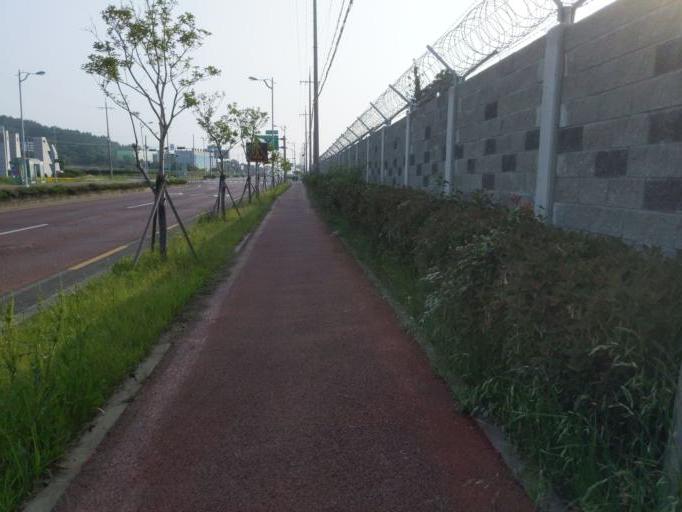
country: KR
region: Jeju-do
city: Gaigeturi
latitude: 33.2297
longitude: 126.2615
